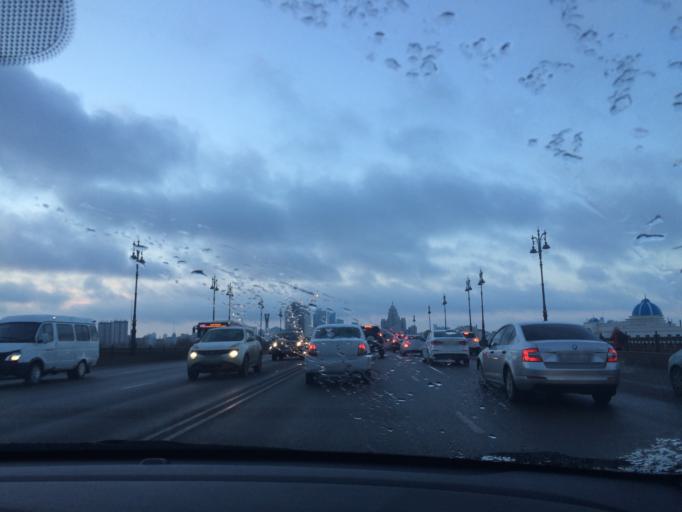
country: KZ
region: Astana Qalasy
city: Astana
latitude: 51.1574
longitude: 71.4113
